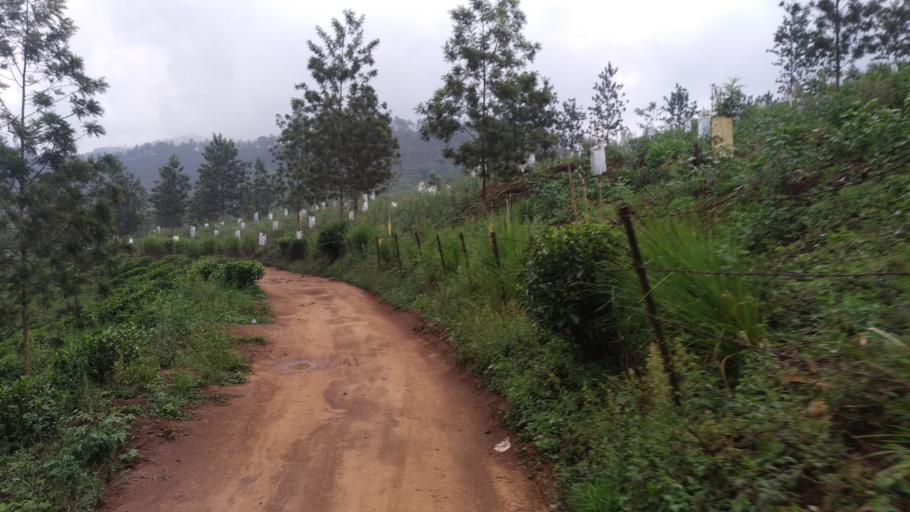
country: IN
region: Tamil Nadu
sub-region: Theni
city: Gudalur
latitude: 9.5670
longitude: 77.0864
